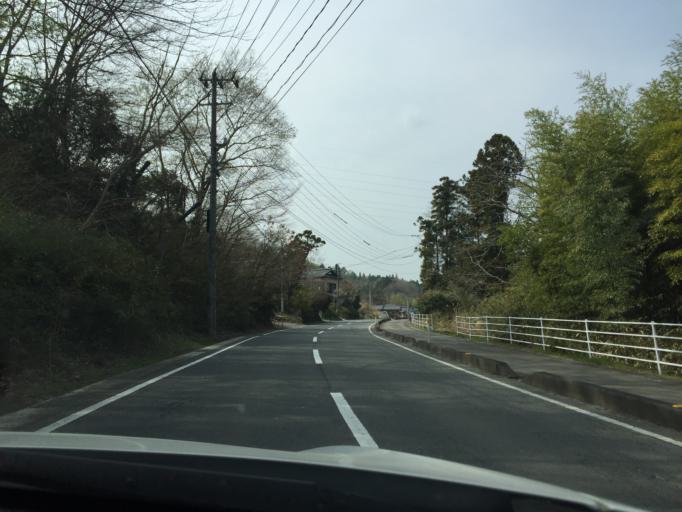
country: JP
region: Fukushima
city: Iwaki
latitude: 37.0186
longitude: 140.7334
